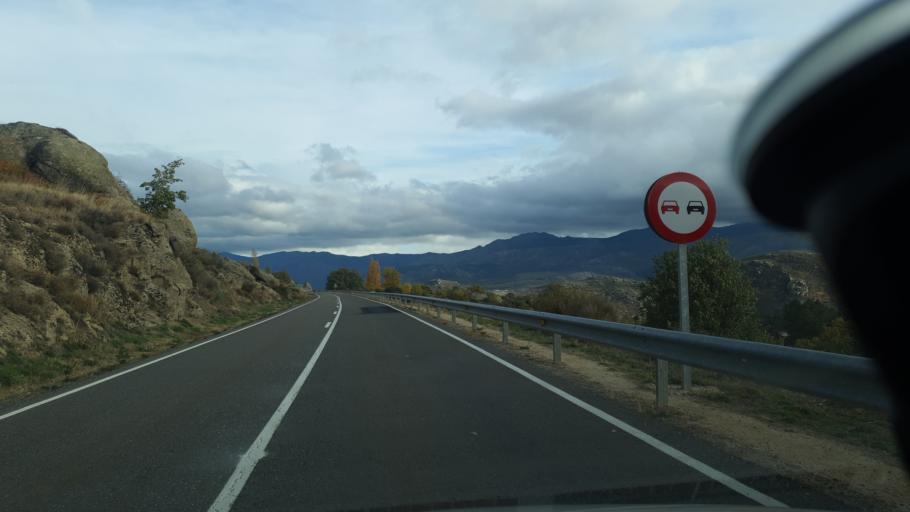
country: ES
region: Castille and Leon
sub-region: Provincia de Avila
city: Navalosa
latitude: 40.3972
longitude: -4.9282
